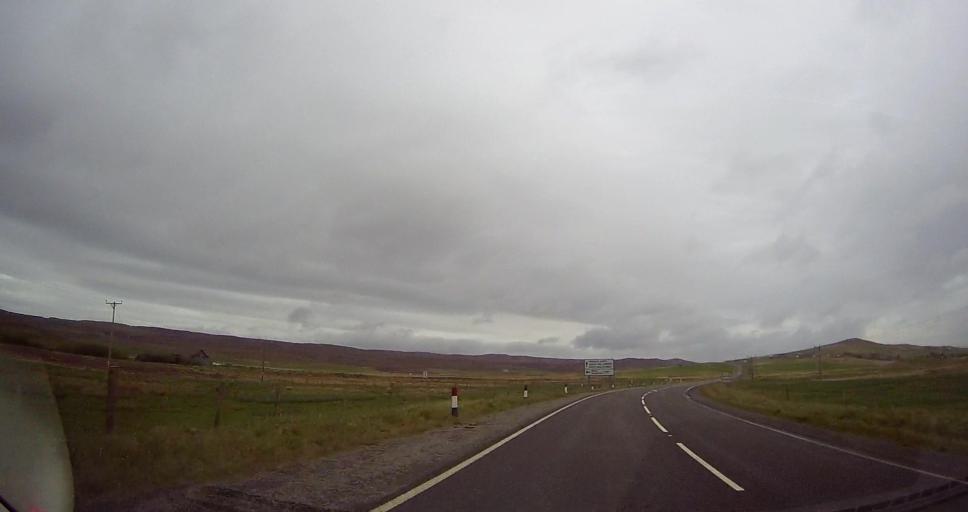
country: GB
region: Scotland
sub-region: Shetland Islands
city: Lerwick
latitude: 60.1889
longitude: -1.2315
